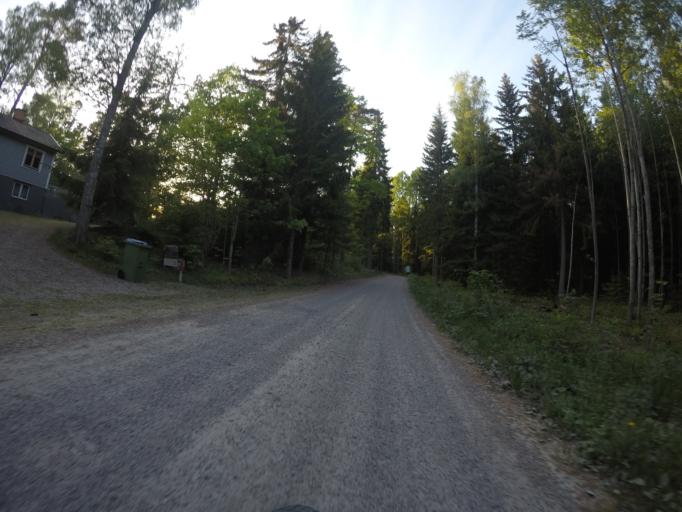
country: SE
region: Soedermanland
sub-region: Eskilstuna Kommun
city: Skogstorp
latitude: 59.3315
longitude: 16.4919
